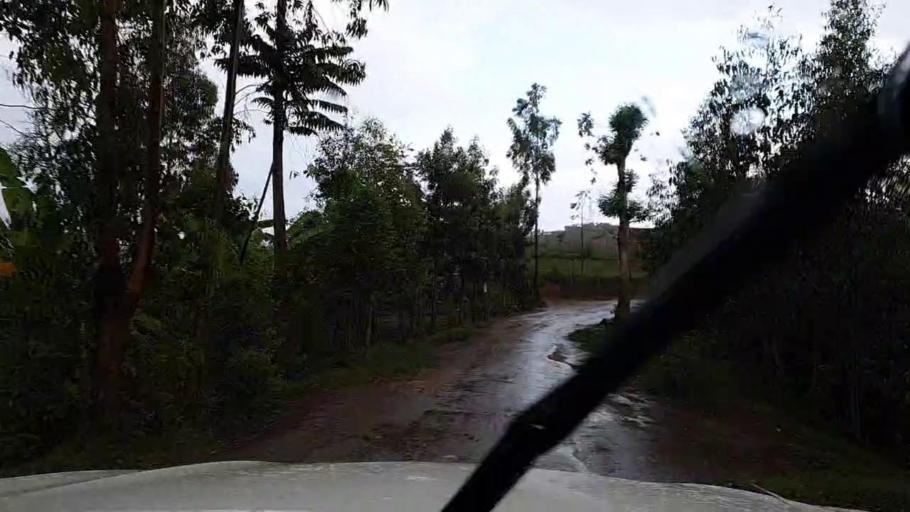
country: BI
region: Kayanza
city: Kayanza
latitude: -2.7727
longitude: 29.5447
